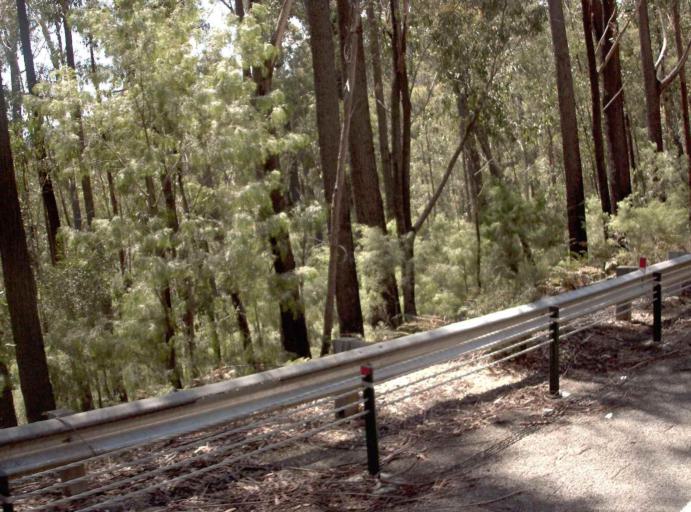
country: AU
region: New South Wales
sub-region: Bombala
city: Bombala
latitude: -37.5871
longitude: 148.9911
